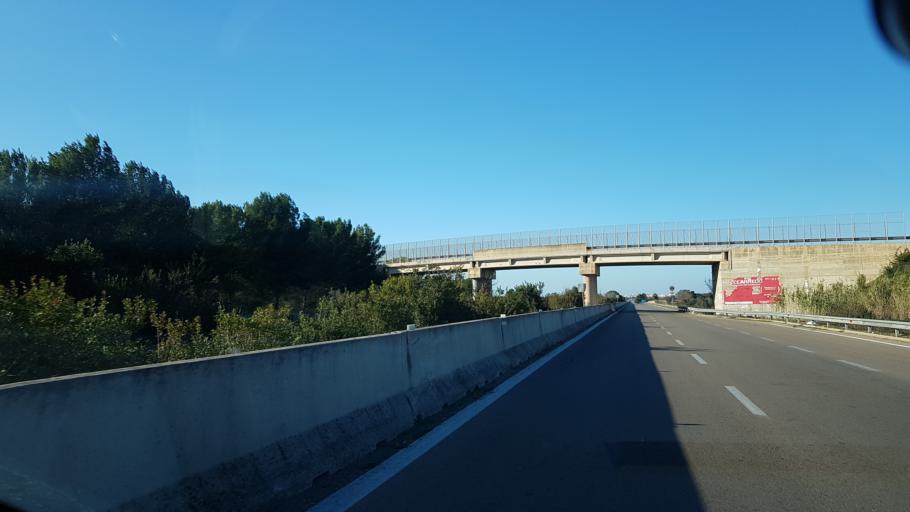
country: IT
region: Apulia
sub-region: Provincia di Lecce
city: Taviano
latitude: 40.0116
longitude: 18.0520
